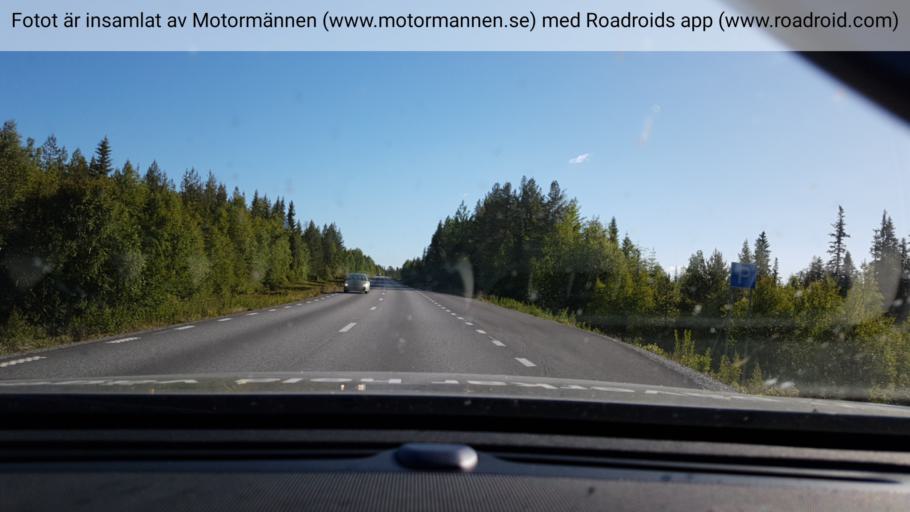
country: SE
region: Vaesterbotten
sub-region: Vilhelmina Kommun
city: Vilhelmina
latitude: 64.7558
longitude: 16.7269
